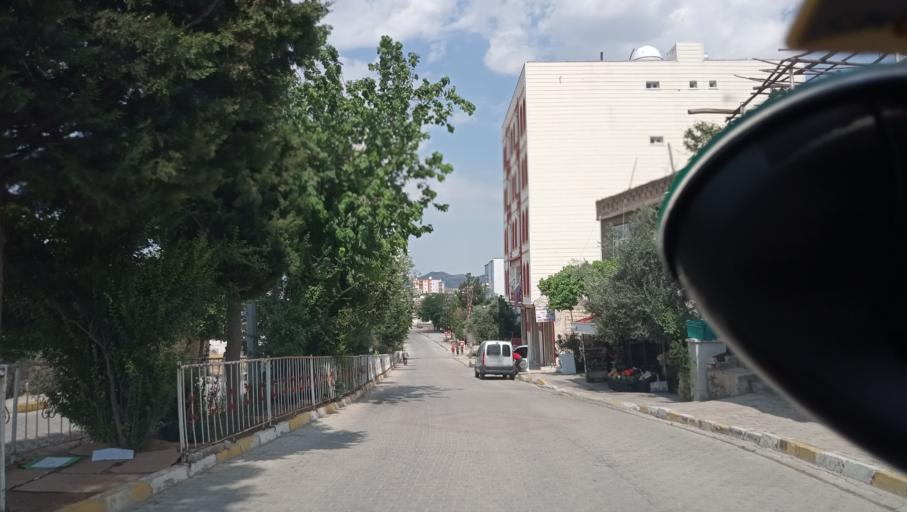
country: TR
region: Mardin
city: Yesilli
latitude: 37.3392
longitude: 40.8198
